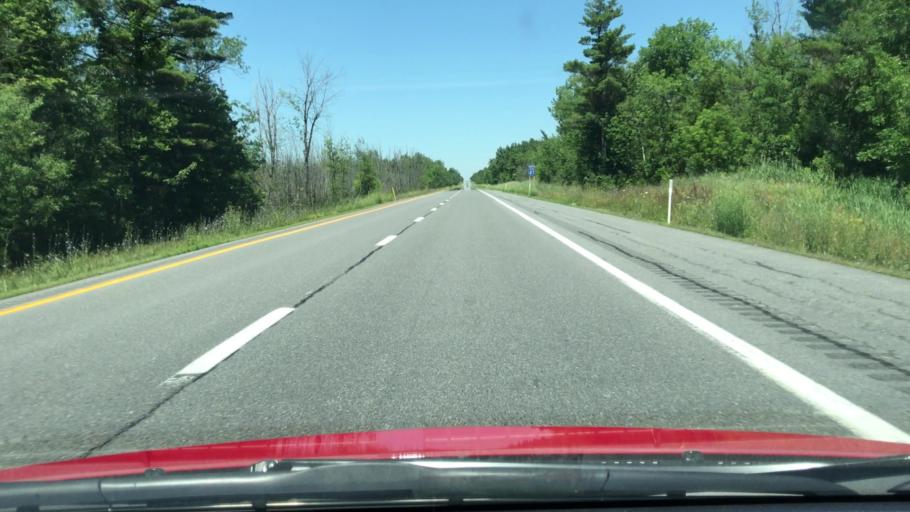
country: US
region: New York
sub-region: Clinton County
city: Champlain
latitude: 44.9410
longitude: -73.4472
